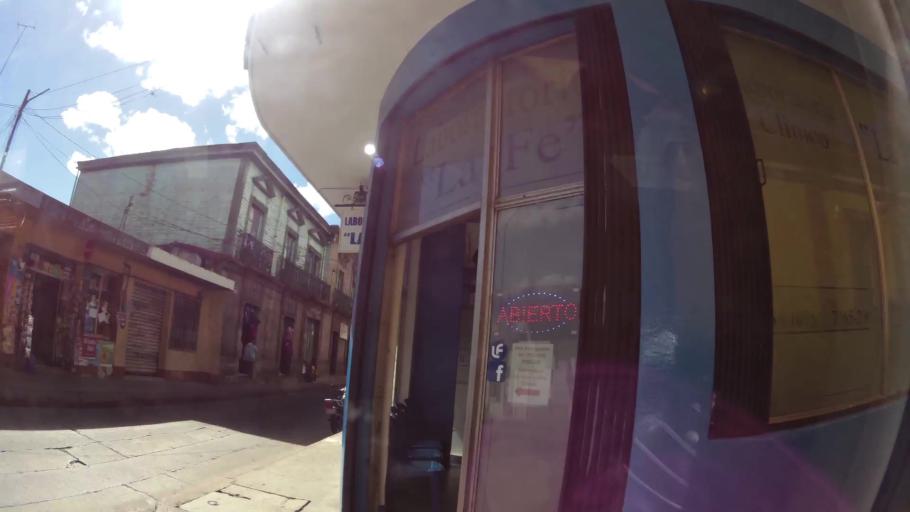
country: GT
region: Quetzaltenango
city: Quetzaltenango
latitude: 14.8376
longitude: -91.5175
